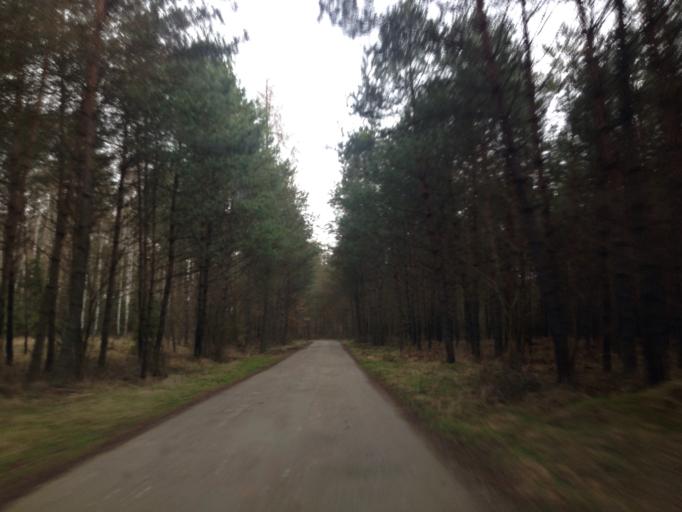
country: PL
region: Kujawsko-Pomorskie
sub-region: Powiat brodnicki
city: Gorzno
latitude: 53.1814
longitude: 19.6760
